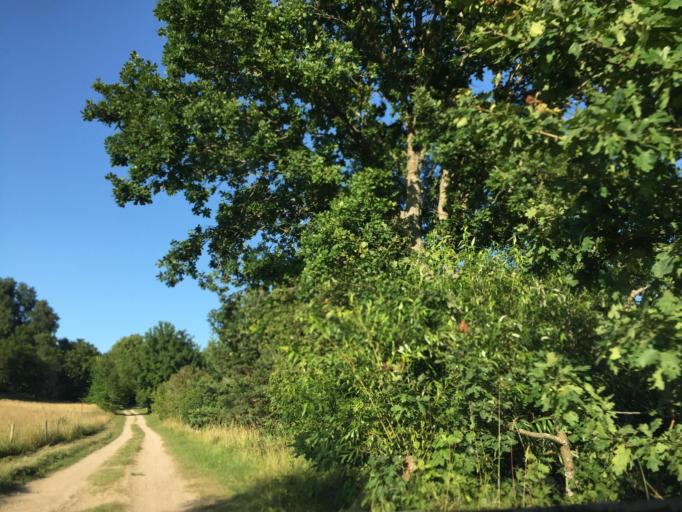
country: LV
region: Kandava
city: Kandava
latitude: 57.0122
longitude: 22.7388
